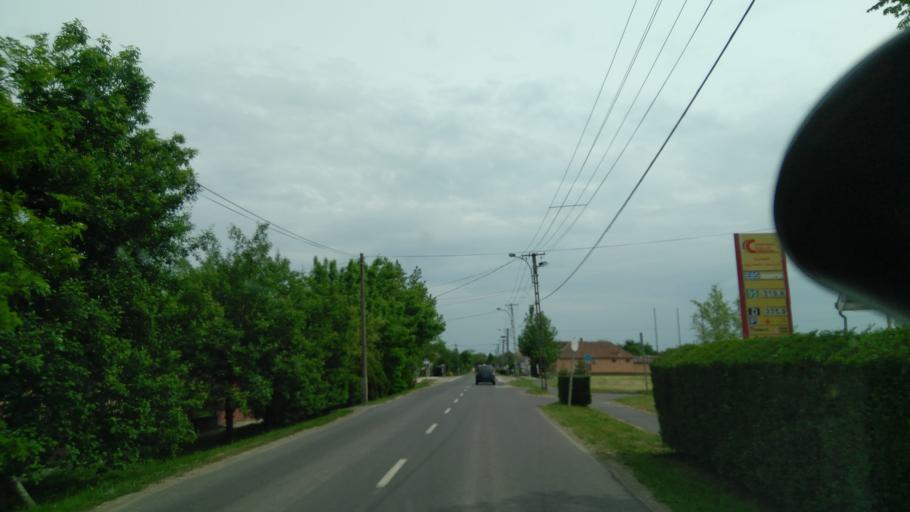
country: HU
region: Bekes
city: Sarkad
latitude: 46.8034
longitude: 21.3836
